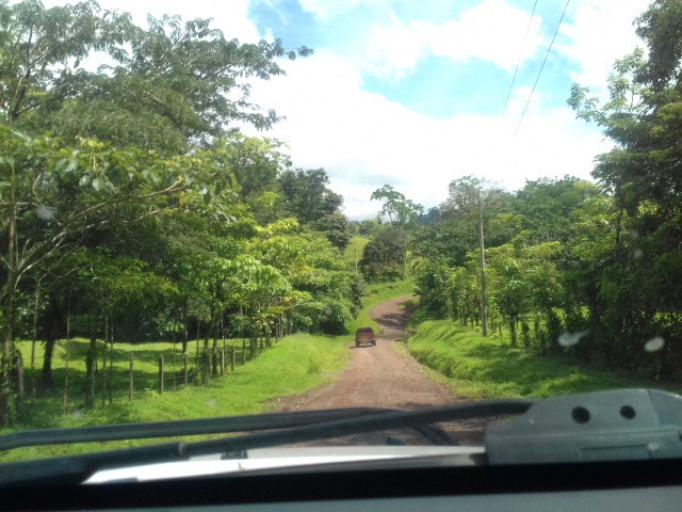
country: NI
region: Matagalpa
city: Rio Blanco
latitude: 12.9874
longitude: -85.1894
